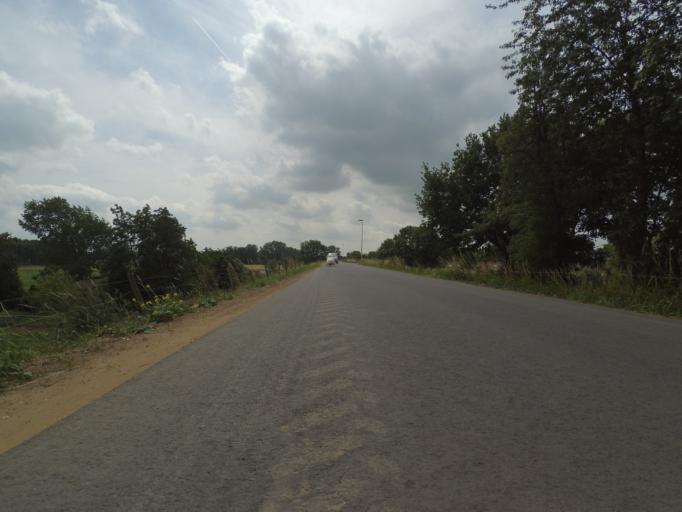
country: NL
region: Gelderland
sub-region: Gemeente Culemborg
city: Culemborg
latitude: 51.9479
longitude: 5.1640
